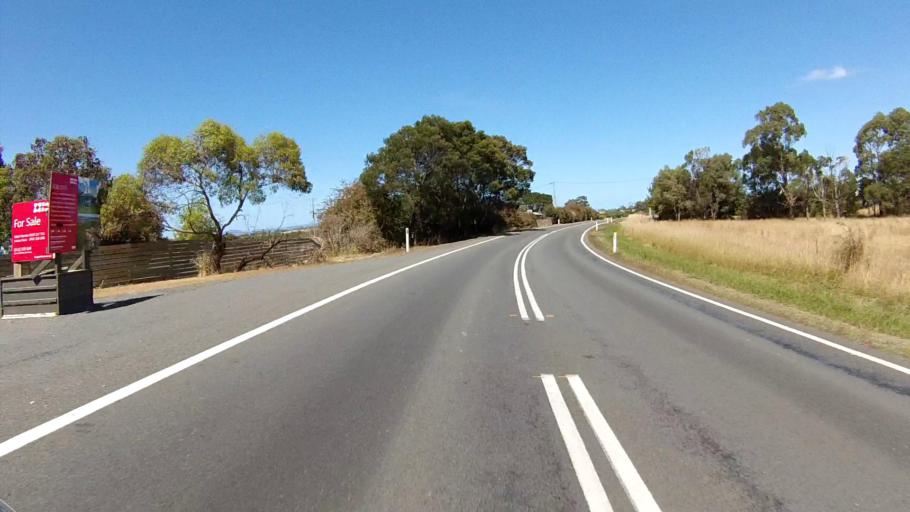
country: AU
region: Tasmania
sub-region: Break O'Day
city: St Helens
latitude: -42.0695
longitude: 148.0653
